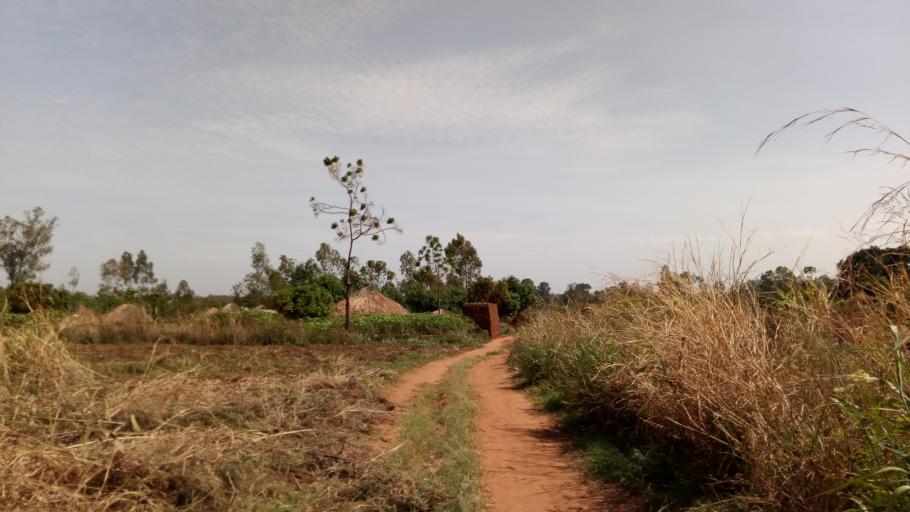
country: UG
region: Northern Region
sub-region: Gulu District
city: Gulu
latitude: 2.7945
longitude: 32.3193
